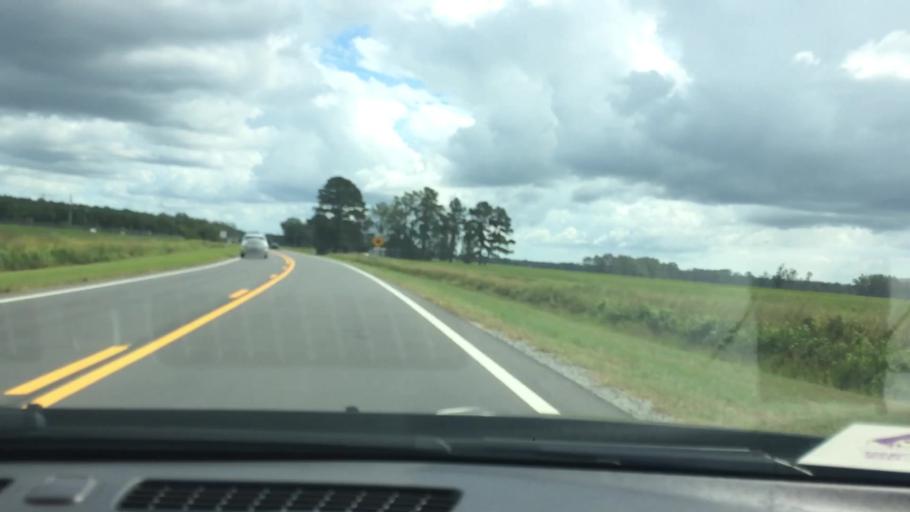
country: US
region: North Carolina
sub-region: Pitt County
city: Farmville
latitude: 35.5500
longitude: -77.5477
